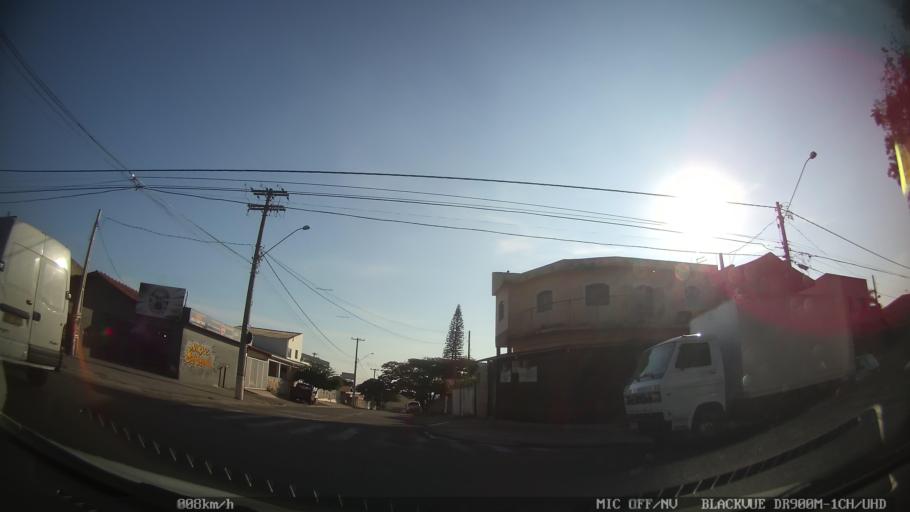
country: BR
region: Sao Paulo
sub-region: Campinas
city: Campinas
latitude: -22.9789
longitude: -47.1479
